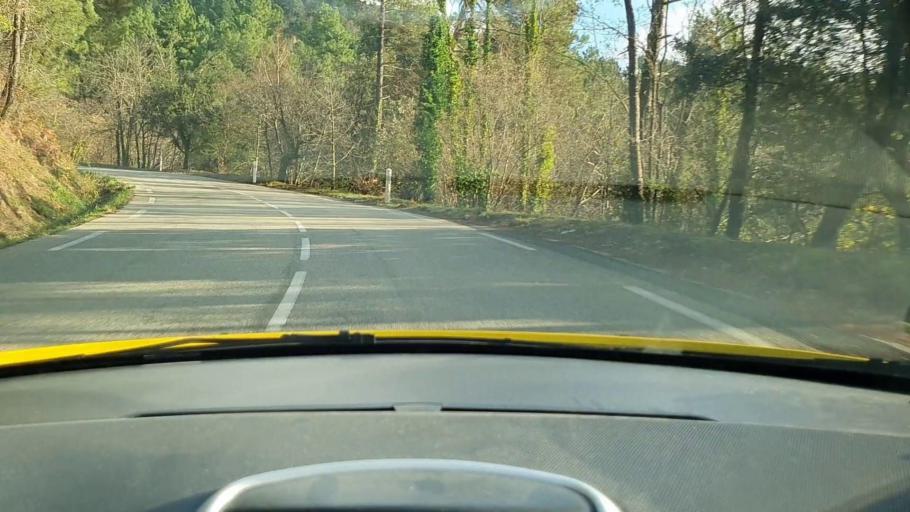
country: FR
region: Languedoc-Roussillon
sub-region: Departement du Gard
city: Branoux-les-Taillades
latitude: 44.2915
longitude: 3.9813
